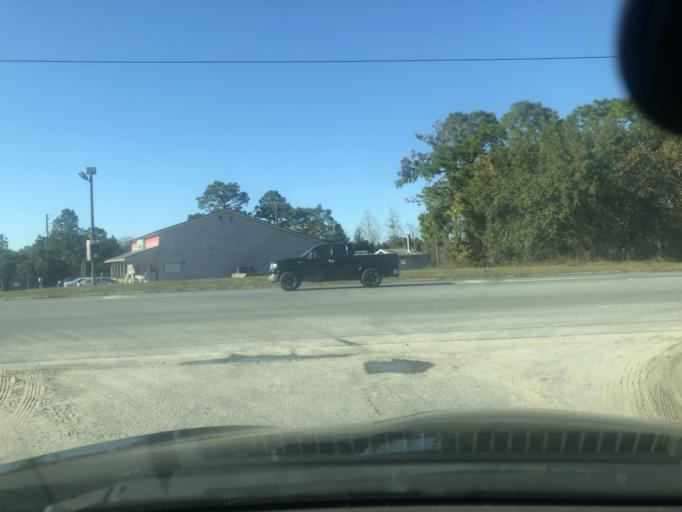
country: US
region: Florida
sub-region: Citrus County
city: Lecanto
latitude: 28.8261
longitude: -82.5254
